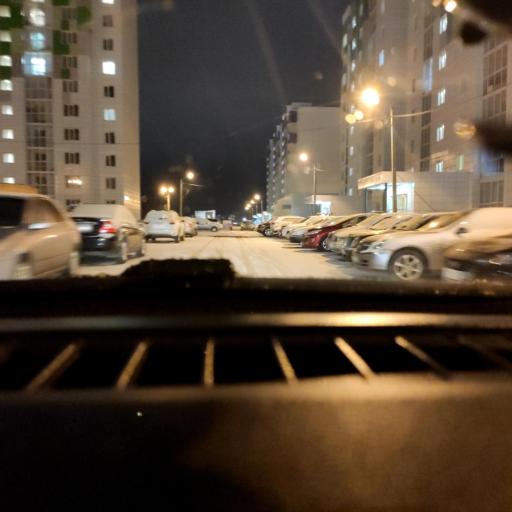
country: RU
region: Voronezj
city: Novaya Usman'
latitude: 51.6492
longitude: 39.3136
